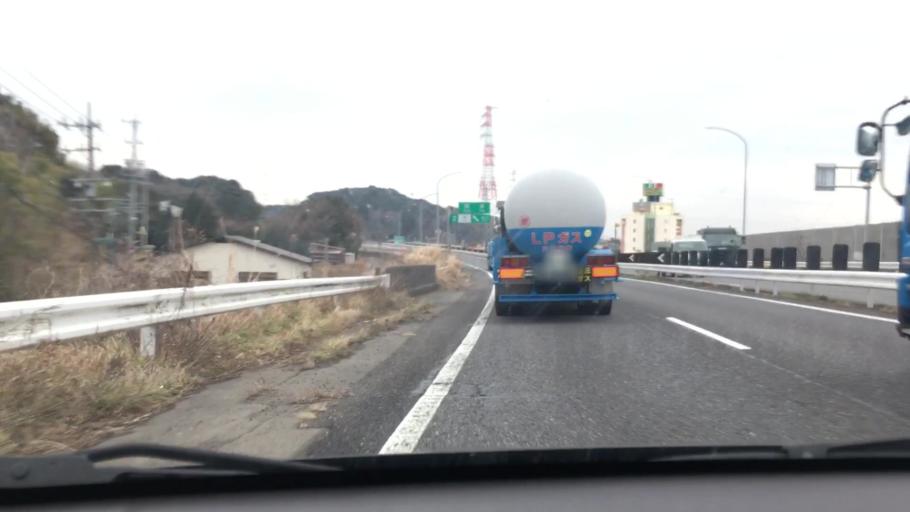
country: JP
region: Mie
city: Kameyama
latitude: 34.8404
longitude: 136.3964
